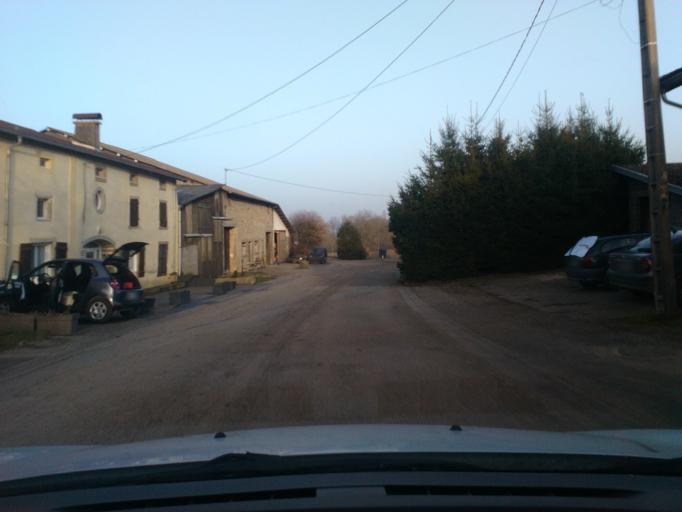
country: FR
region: Lorraine
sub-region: Departement des Vosges
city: Vittel
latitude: 48.2566
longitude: 6.0112
